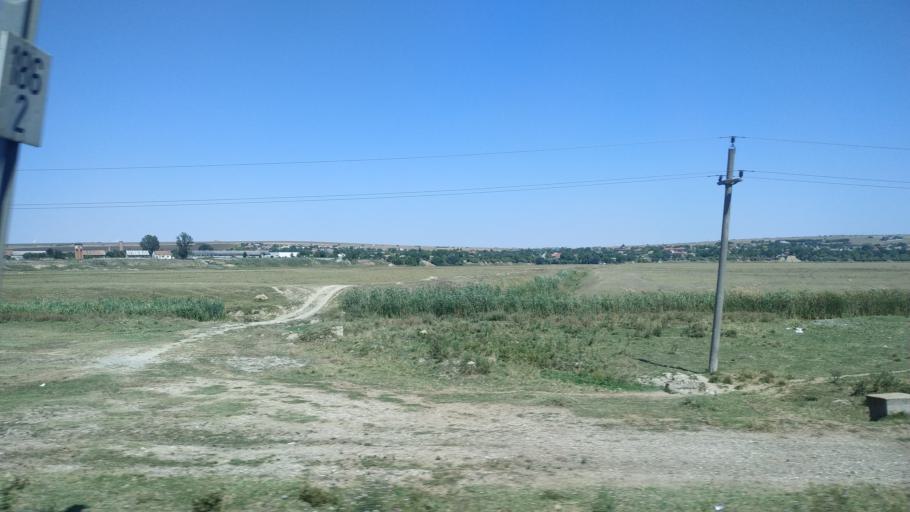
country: RO
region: Constanta
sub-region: Comuna Mircea Voda
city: Satu Nou
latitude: 44.2589
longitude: 28.2194
